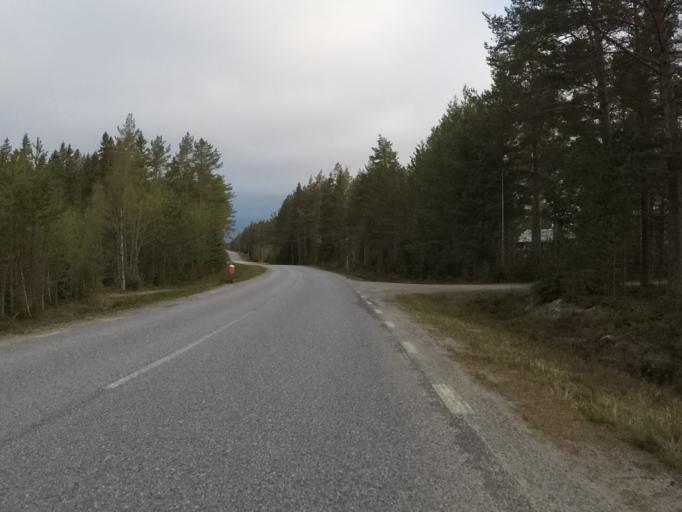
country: SE
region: Vaesterbotten
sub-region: Robertsfors Kommun
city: Robertsfors
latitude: 63.9532
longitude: 20.7946
